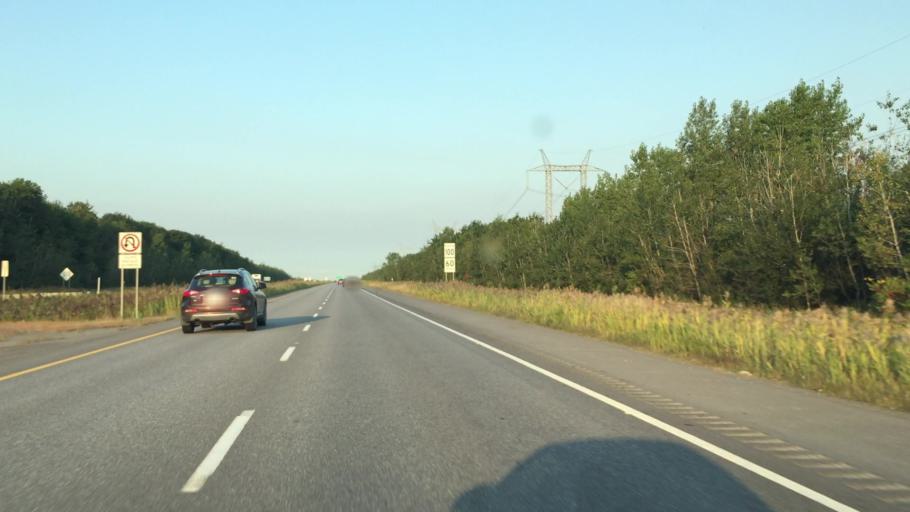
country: CA
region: Quebec
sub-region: Monteregie
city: Richelieu
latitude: 45.4139
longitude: -73.2557
